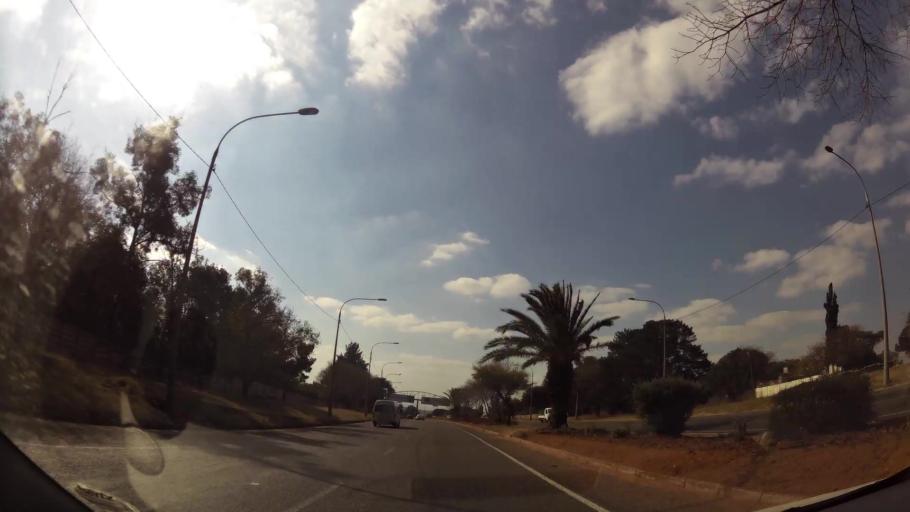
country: ZA
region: Gauteng
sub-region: West Rand District Municipality
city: Krugersdorp
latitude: -26.0838
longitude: 27.7888
